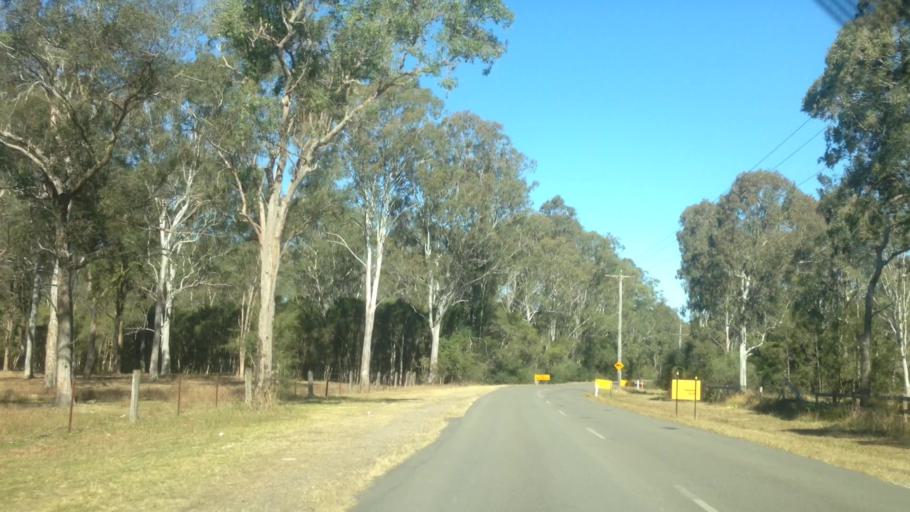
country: AU
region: New South Wales
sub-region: Lake Macquarie Shire
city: Cooranbong
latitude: -33.0954
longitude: 151.4523
